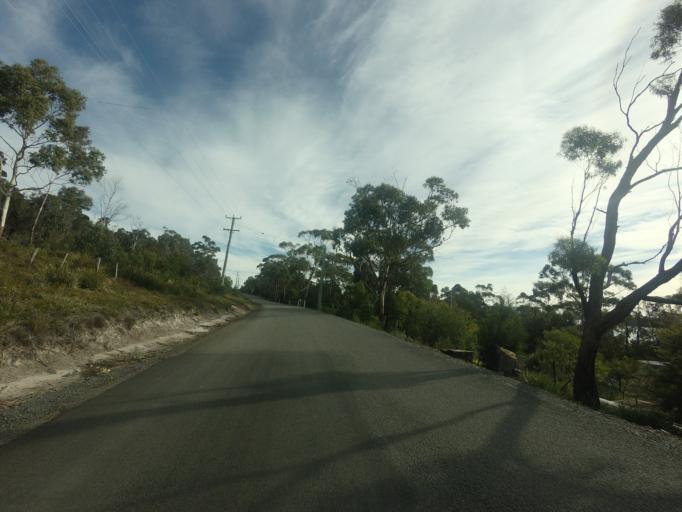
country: AU
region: Tasmania
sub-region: Sorell
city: Sorell
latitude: -42.9584
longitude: 147.8419
